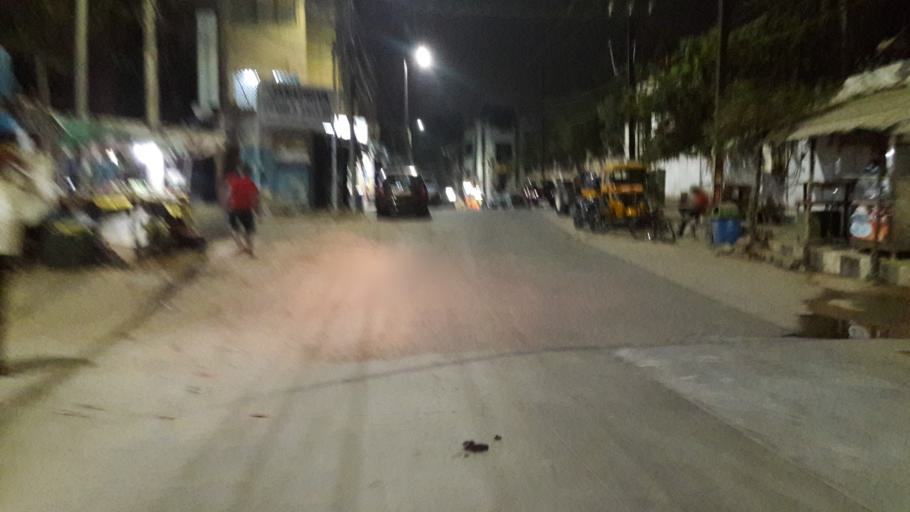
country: IN
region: Telangana
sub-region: Hyderabad
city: Hyderabad
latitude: 17.4358
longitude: 78.4611
